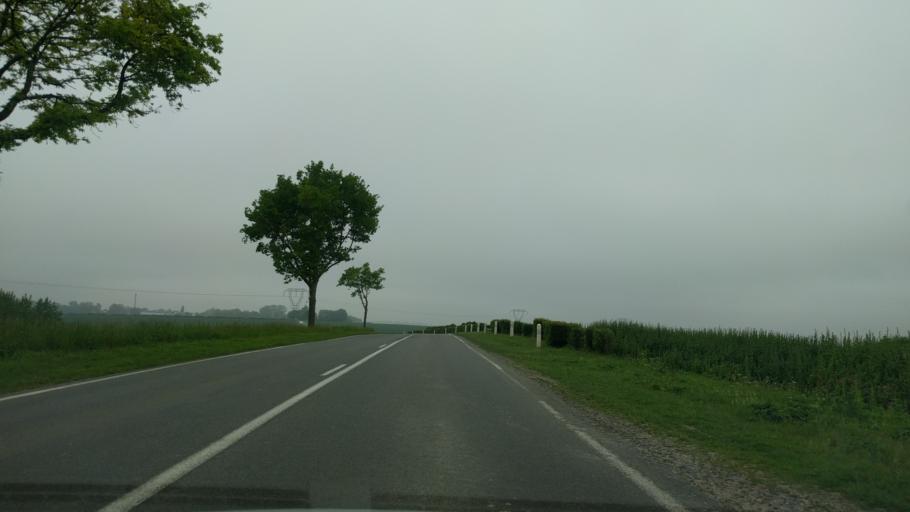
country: FR
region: Picardie
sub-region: Departement de la Somme
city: Moislains
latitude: 50.0460
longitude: 2.9088
